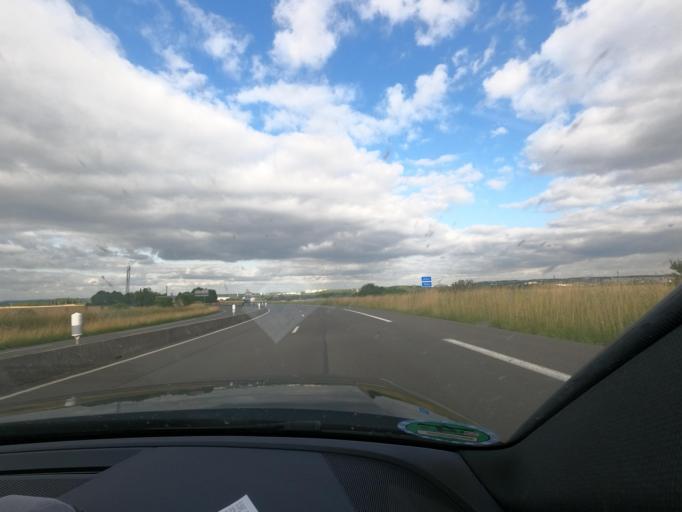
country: FR
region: Picardie
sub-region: Departement de la Somme
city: Pont-de-Metz
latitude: 49.8909
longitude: 2.2341
